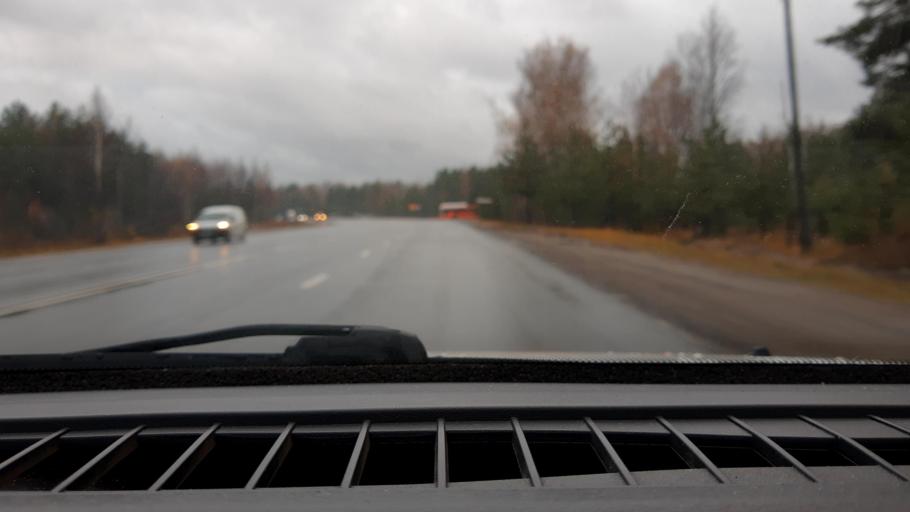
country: RU
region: Nizjnij Novgorod
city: Gorbatovka
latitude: 56.3291
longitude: 43.7834
